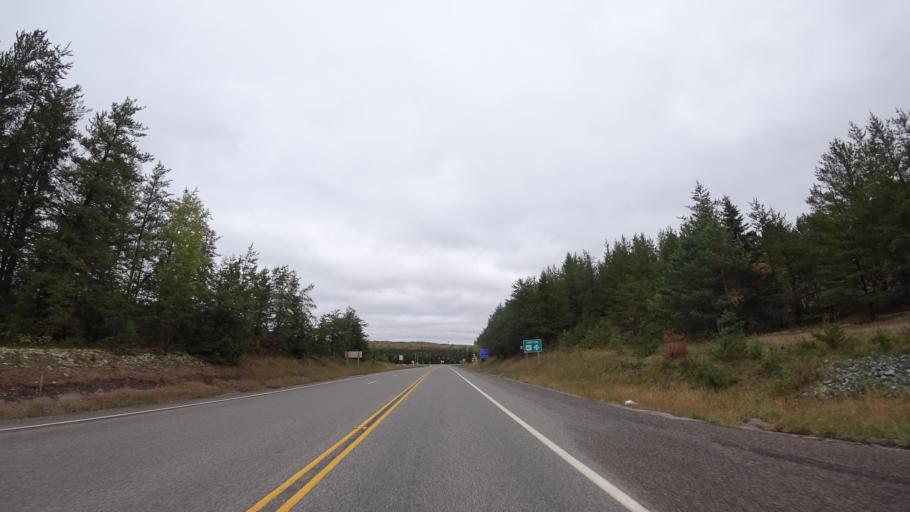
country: US
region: Michigan
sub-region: Marquette County
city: West Ishpeming
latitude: 46.4943
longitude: -87.9193
